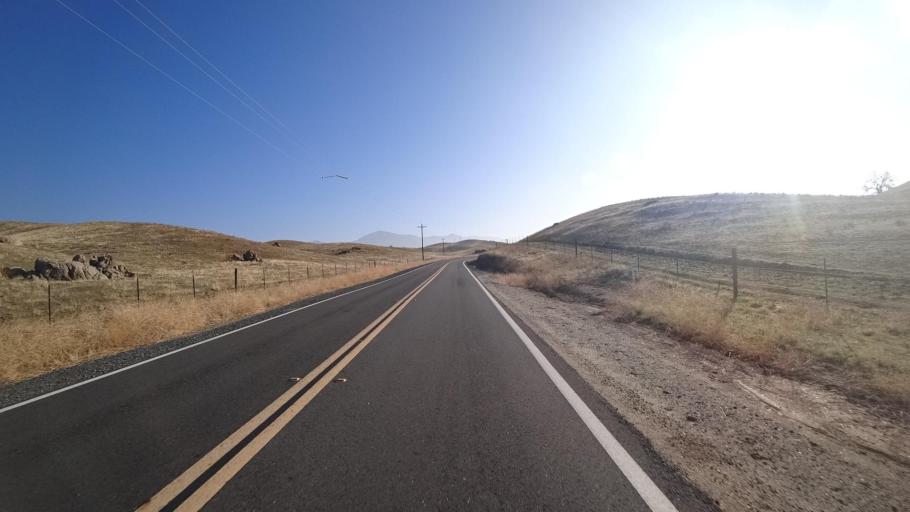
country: US
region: California
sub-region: Tulare County
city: Richgrove
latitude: 35.7421
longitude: -118.8899
